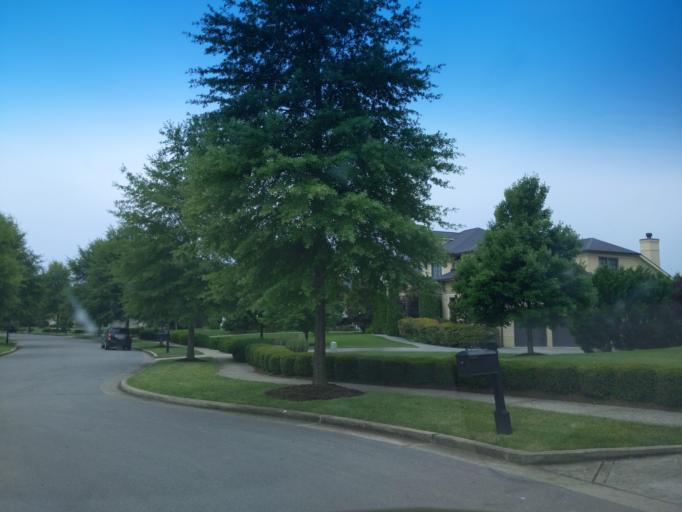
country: US
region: Tennessee
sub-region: Williamson County
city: Brentwood Estates
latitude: 36.0294
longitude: -86.7714
